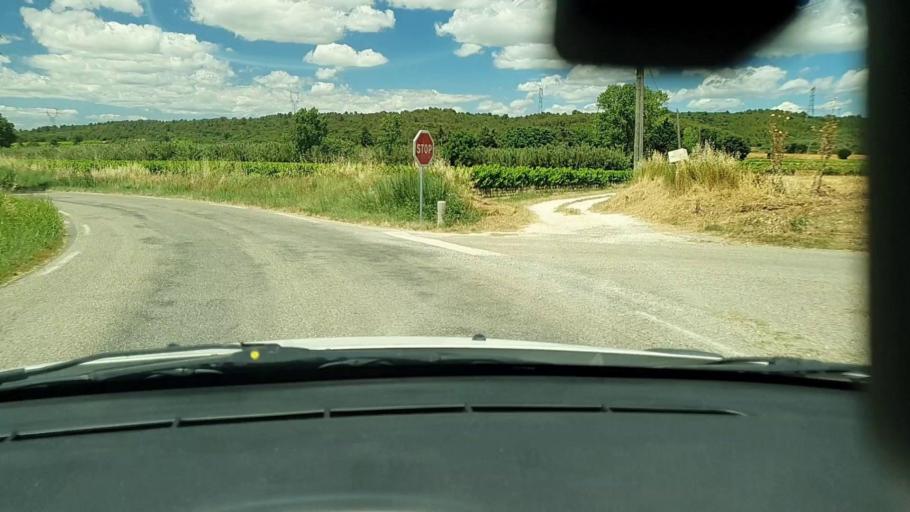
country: FR
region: Languedoc-Roussillon
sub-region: Departement du Gard
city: Poulx
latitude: 43.9526
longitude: 4.4141
